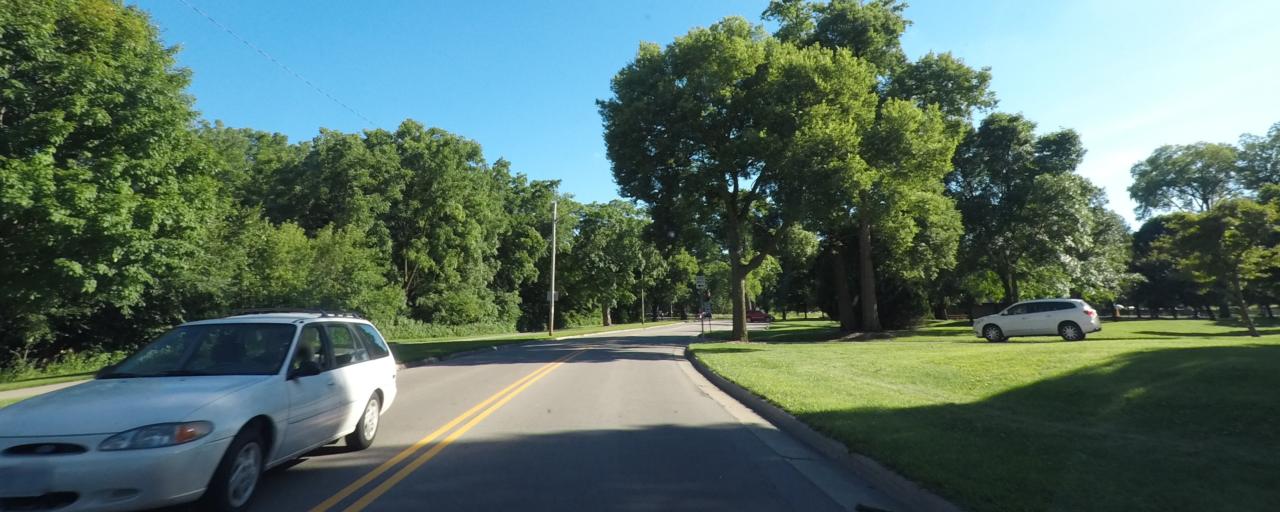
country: US
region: Wisconsin
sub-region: Rock County
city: Janesville
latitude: 42.6779
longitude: -88.9905
